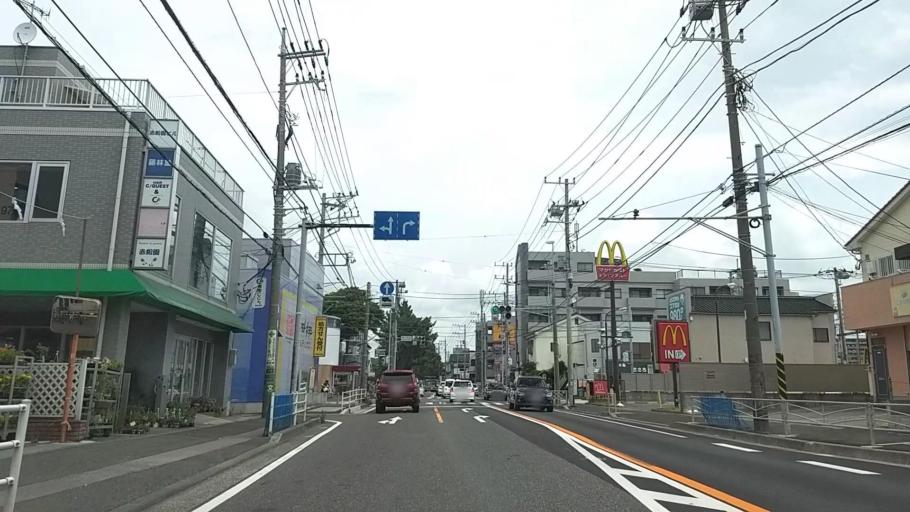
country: JP
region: Kanagawa
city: Fujisawa
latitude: 35.3412
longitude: 139.4374
